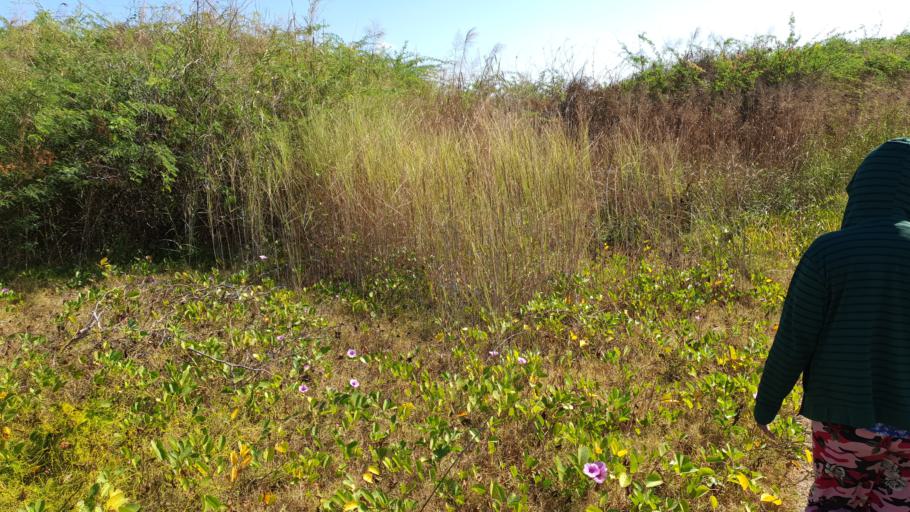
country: PH
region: Ilocos
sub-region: Province of La Union
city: Payocpoc Sur
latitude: 16.5016
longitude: 120.3052
